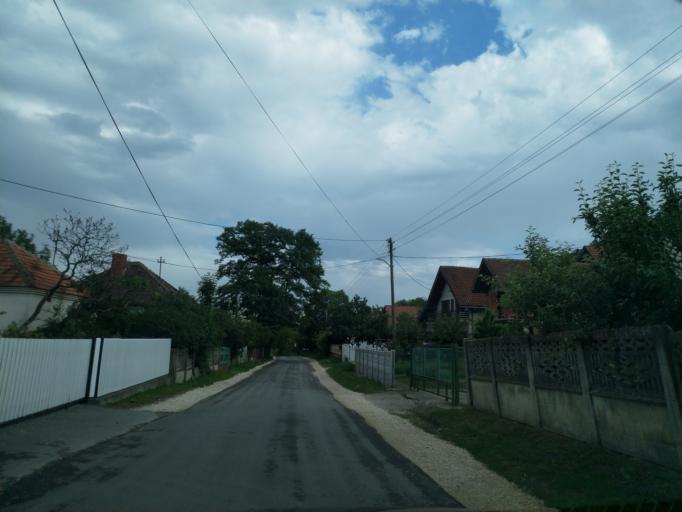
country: RS
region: Central Serbia
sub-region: Borski Okrug
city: Bor
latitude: 44.0157
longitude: 21.9823
